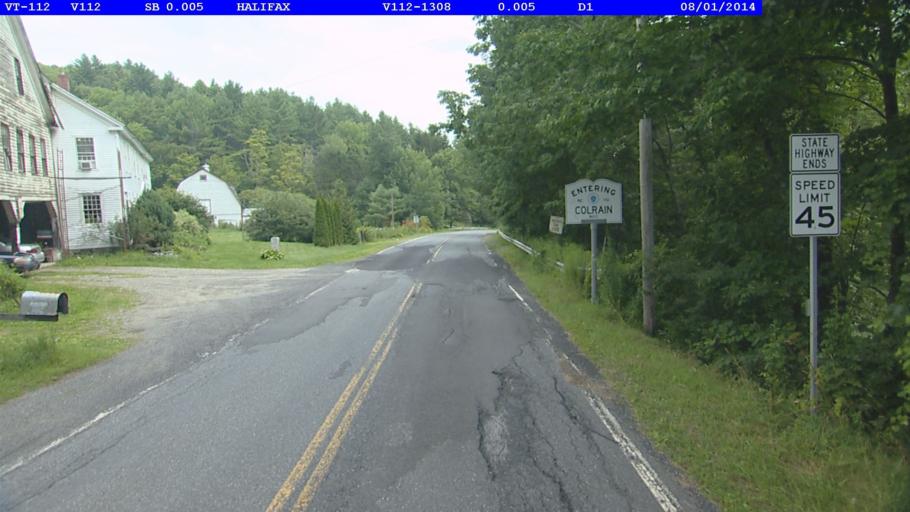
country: US
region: Massachusetts
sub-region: Franklin County
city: Colrain
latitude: 42.7343
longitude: -72.7218
